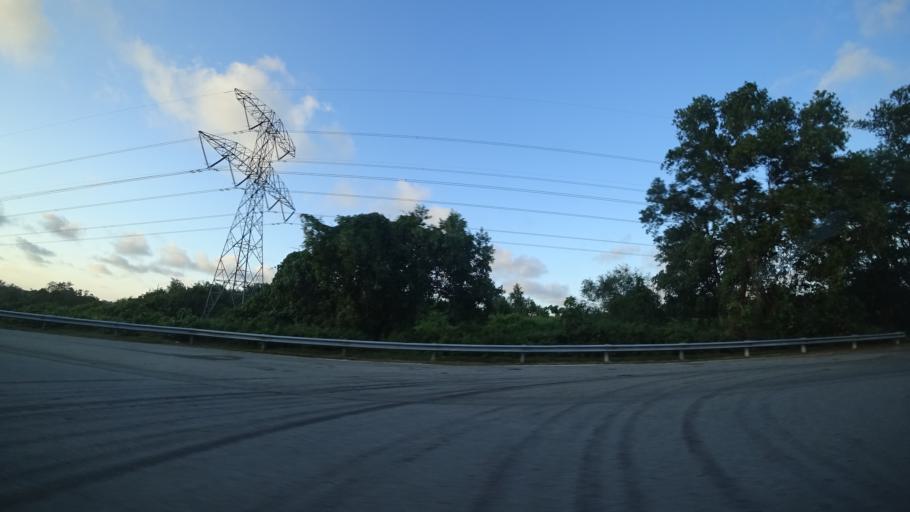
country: BN
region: Tutong
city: Tutong
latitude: 4.8307
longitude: 114.7219
